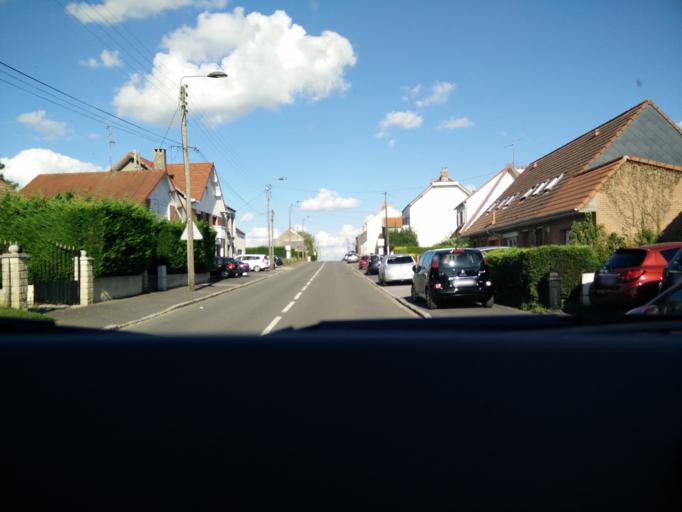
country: FR
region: Nord-Pas-de-Calais
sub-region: Departement du Nord
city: Rousies
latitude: 50.2845
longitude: 3.9914
